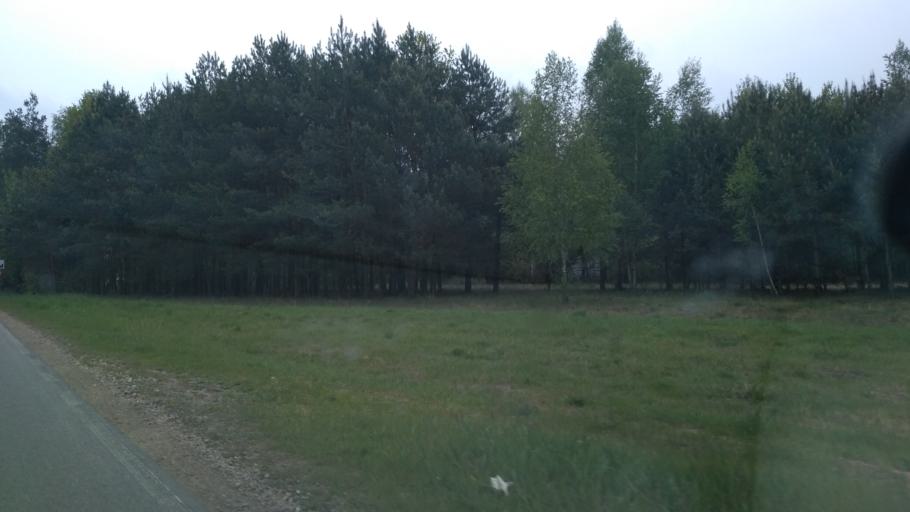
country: PL
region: Subcarpathian Voivodeship
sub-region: Powiat ropczycko-sedziszowski
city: Sedziszow Malopolski
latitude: 50.1204
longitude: 21.7506
